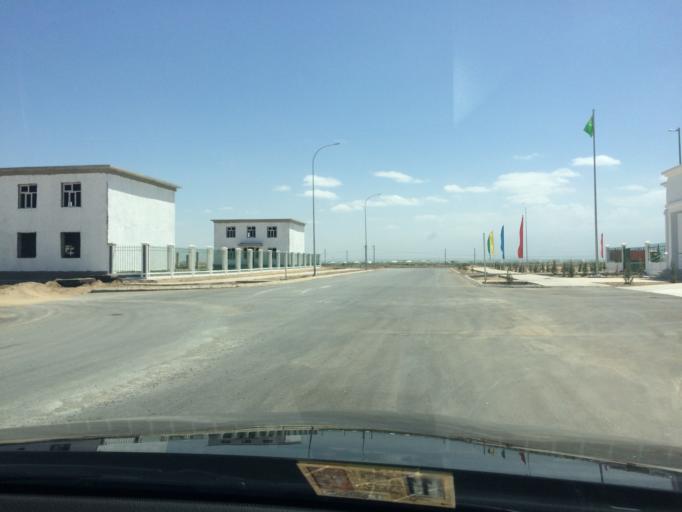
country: TM
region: Ahal
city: Abadan
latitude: 38.0942
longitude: 58.2940
